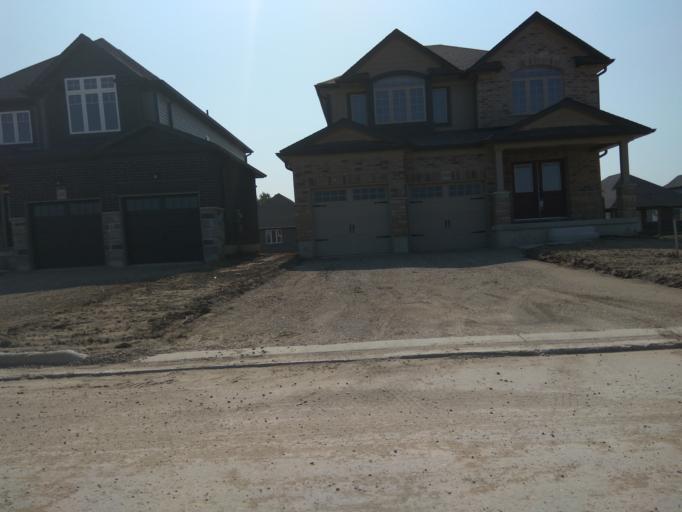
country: CA
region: Ontario
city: Stratford
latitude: 43.3860
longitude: -80.9873
